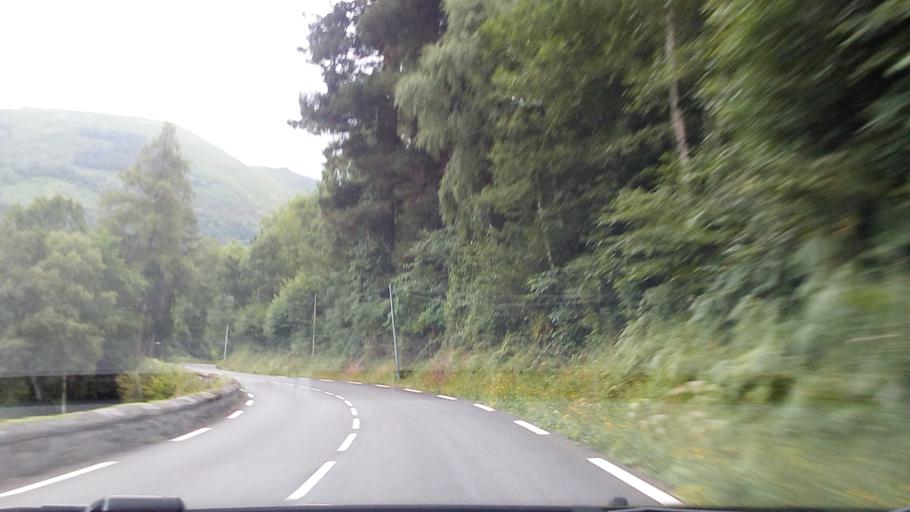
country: FR
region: Aquitaine
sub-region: Departement des Pyrenees-Atlantiques
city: Laruns
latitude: 42.9777
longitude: -0.4138
